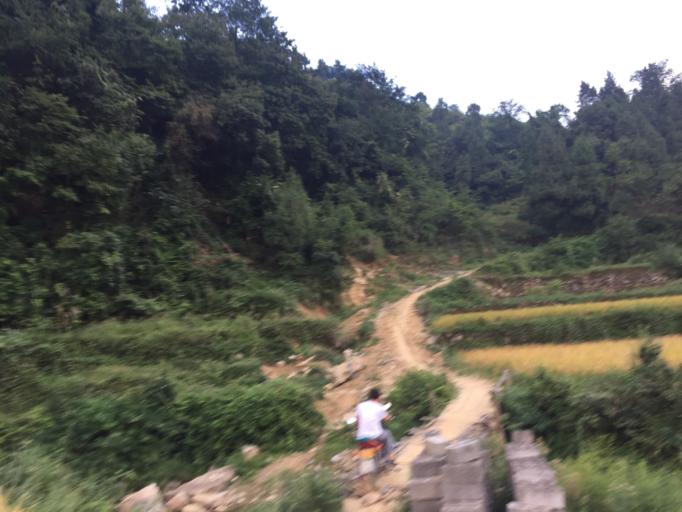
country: CN
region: Guizhou Sheng
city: Shiqian
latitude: 27.6071
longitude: 107.9949
